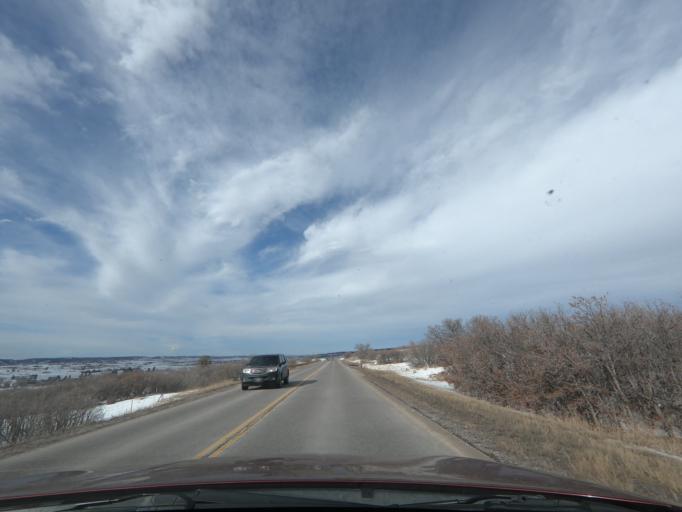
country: US
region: Colorado
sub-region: Douglas County
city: The Pinery
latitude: 39.3638
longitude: -104.7477
